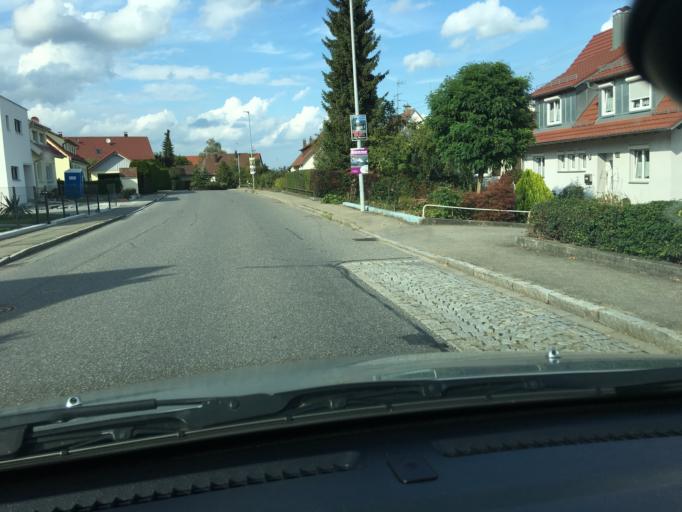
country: DE
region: Baden-Wuerttemberg
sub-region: Tuebingen Region
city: Aulendorf
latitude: 47.9738
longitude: 9.6431
